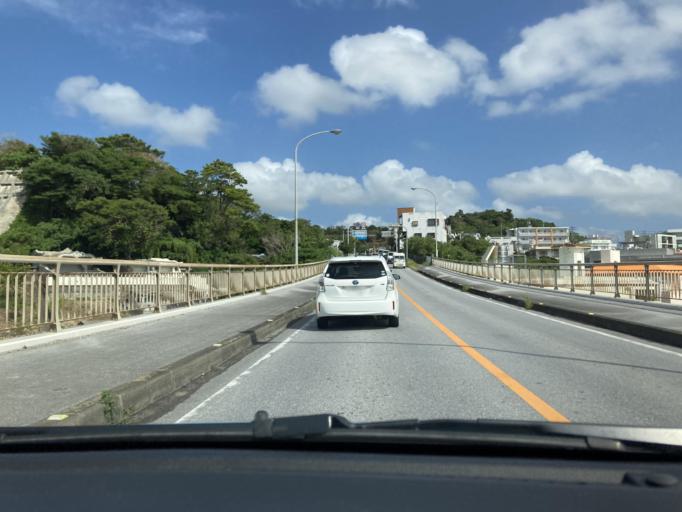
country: JP
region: Okinawa
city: Chatan
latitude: 26.2941
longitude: 127.7846
